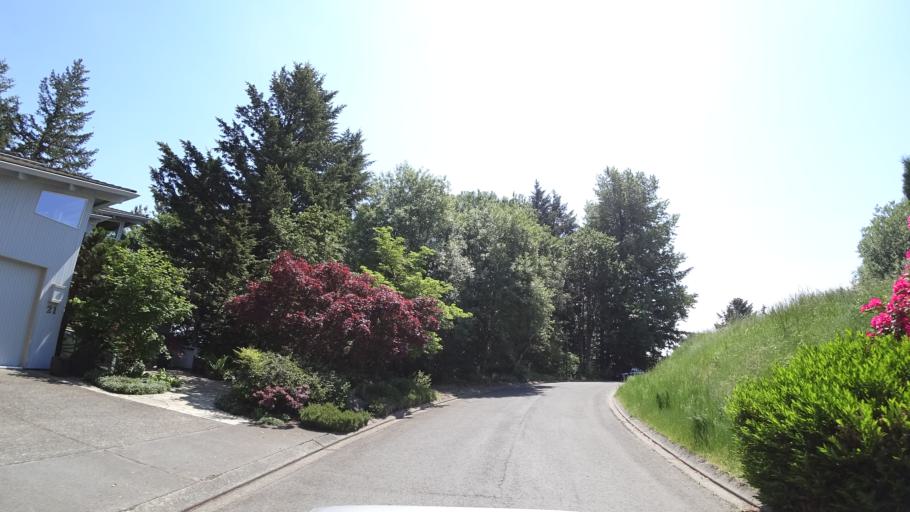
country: US
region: Oregon
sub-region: Washington County
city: Metzger
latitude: 45.4381
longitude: -122.7212
